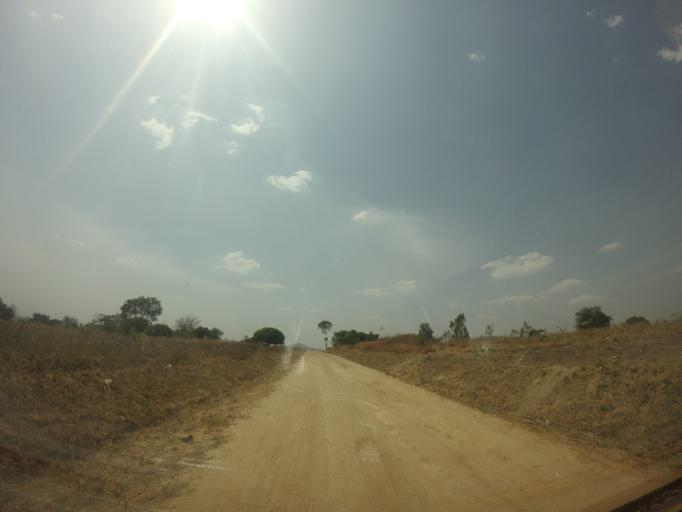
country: UG
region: Northern Region
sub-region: Arua District
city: Arua
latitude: 2.9124
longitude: 31.0467
